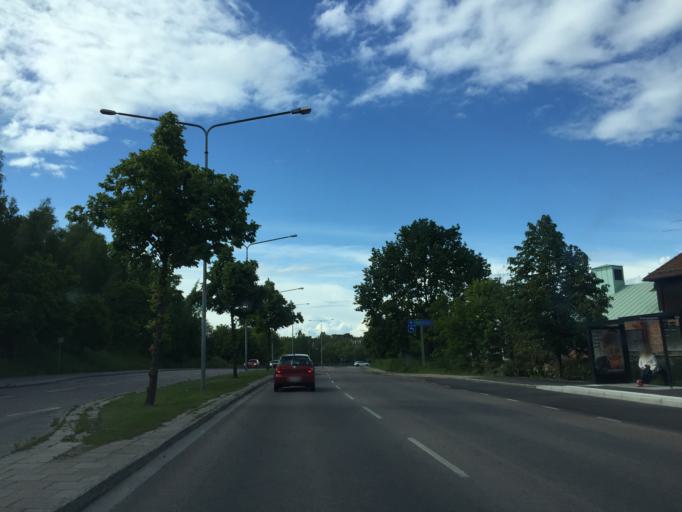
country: SE
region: Vaestmanland
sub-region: Vasteras
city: Vasteras
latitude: 59.6117
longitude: 16.5356
